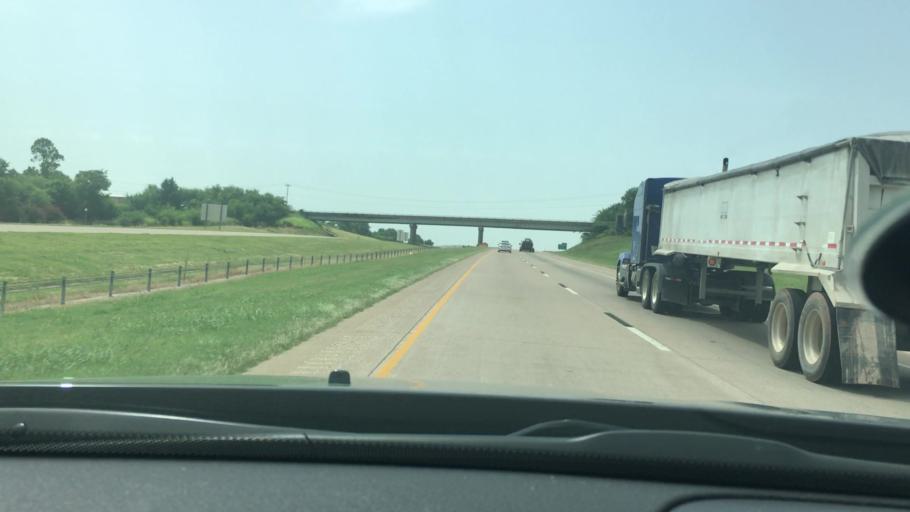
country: US
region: Oklahoma
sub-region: Garvin County
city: Pauls Valley
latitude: 34.7265
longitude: -97.2549
